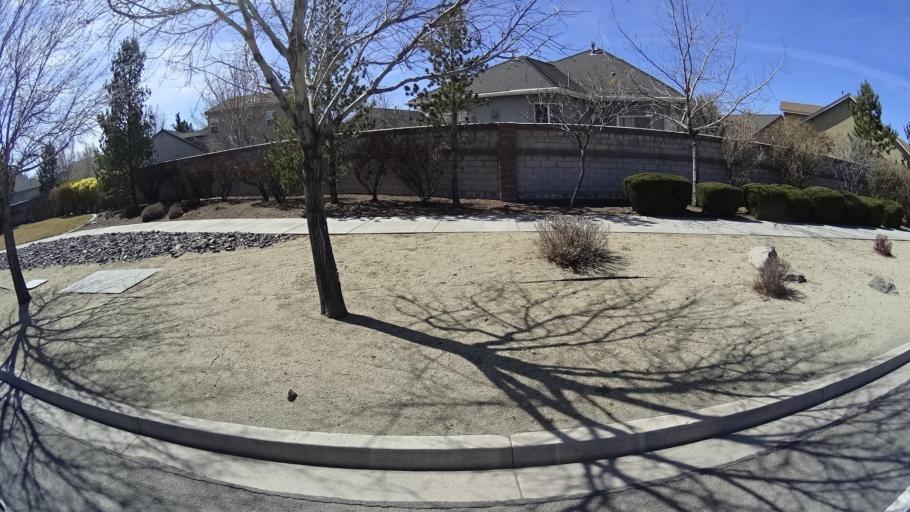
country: US
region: Nevada
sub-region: Washoe County
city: Sun Valley
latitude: 39.5883
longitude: -119.7263
